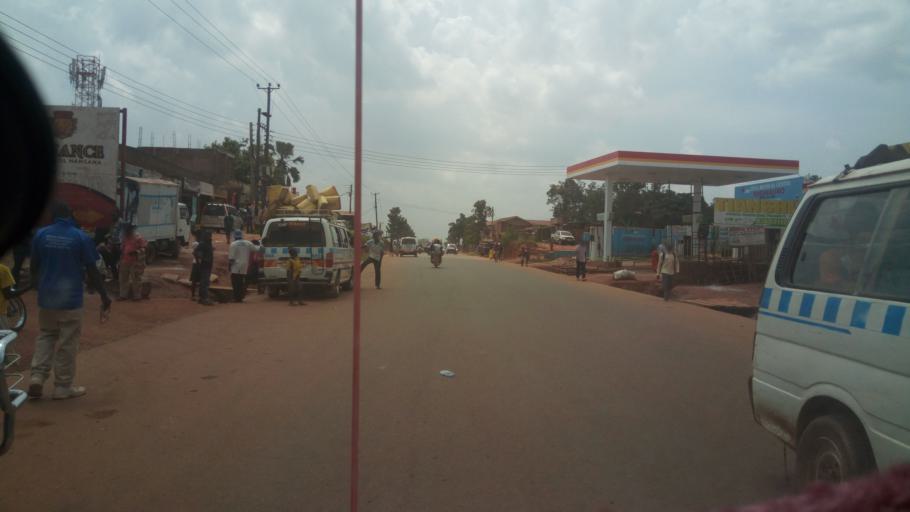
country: UG
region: Central Region
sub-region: Wakiso District
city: Wakiso
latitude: 0.3781
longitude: 32.5200
